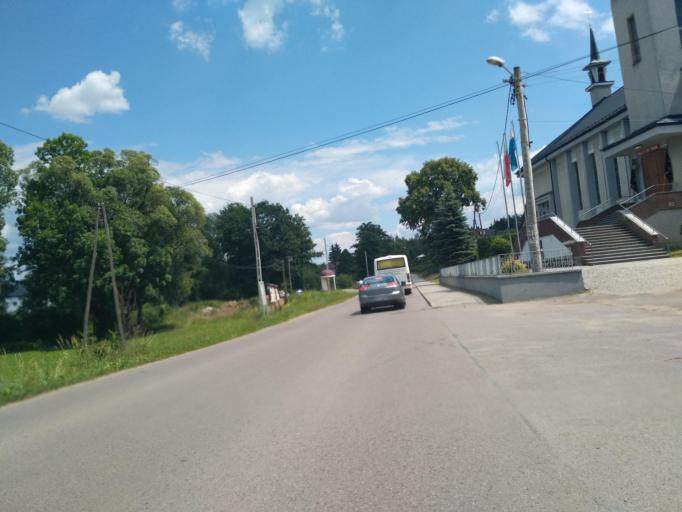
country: PL
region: Subcarpathian Voivodeship
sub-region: Powiat debicki
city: Brzostek
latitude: 49.8619
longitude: 21.4497
